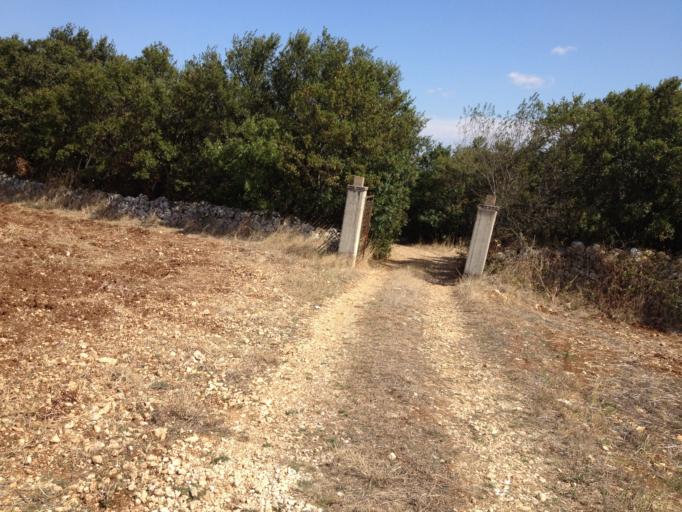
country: IT
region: Apulia
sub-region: Provincia di Bari
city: Gioia del Colle
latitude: 40.8213
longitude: 16.9988
